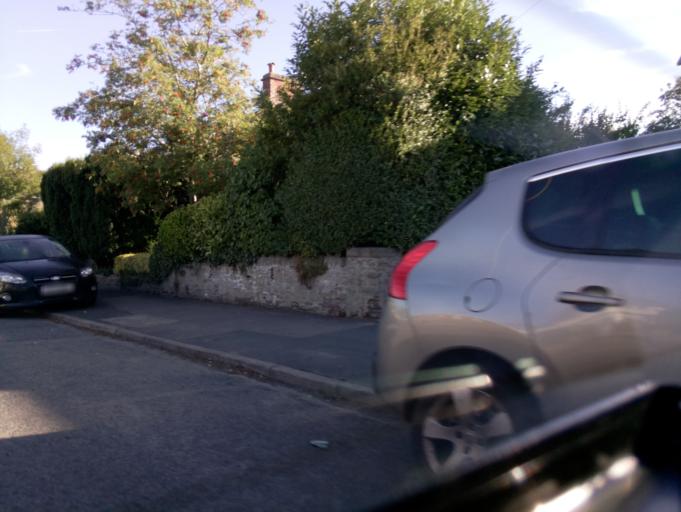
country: GB
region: England
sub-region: South Gloucestershire
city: Kingswood
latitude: 51.4371
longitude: -2.4923
